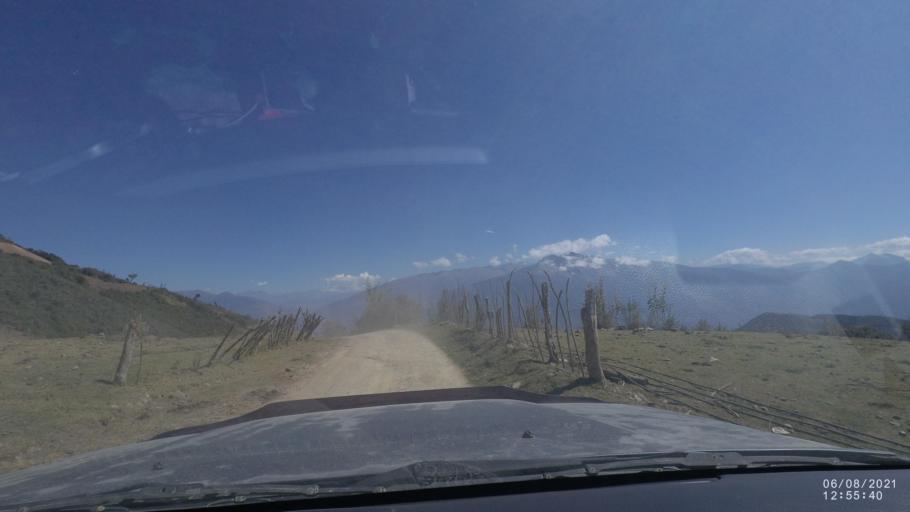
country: BO
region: Cochabamba
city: Colchani
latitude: -16.7553
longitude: -66.6835
